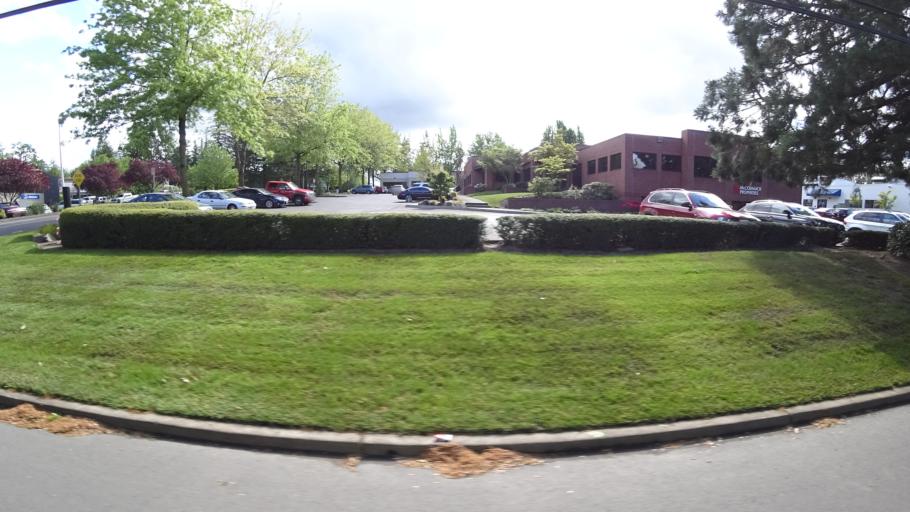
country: US
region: Oregon
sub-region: Washington County
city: Durham
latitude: 45.4211
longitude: -122.7518
